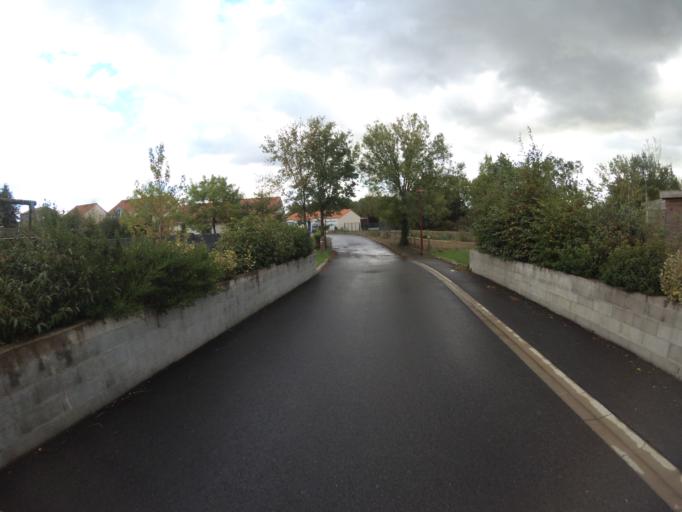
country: FR
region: Pays de la Loire
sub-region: Departement de la Loire-Atlantique
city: Saint-Hilaire-de-Clisson
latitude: 47.0660
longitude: -1.3136
